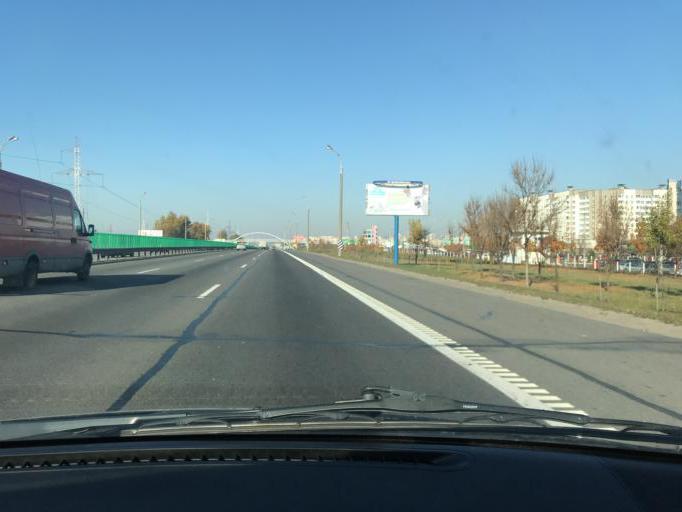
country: BY
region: Minsk
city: Malinovka
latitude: 53.8604
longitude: 27.4277
